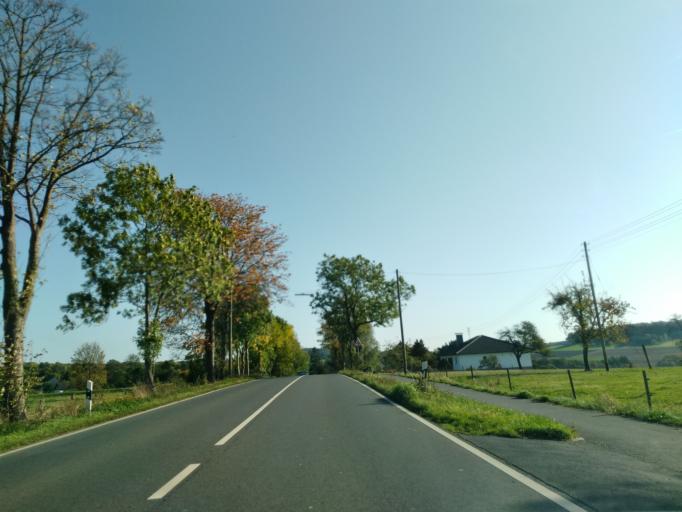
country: DE
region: Rheinland-Pfalz
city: Asbach
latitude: 50.7245
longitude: 7.3744
